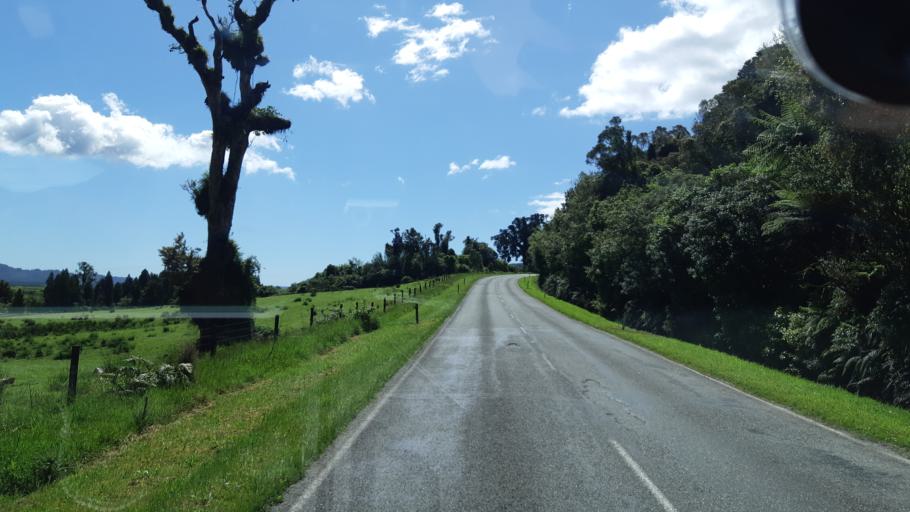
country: NZ
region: West Coast
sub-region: Westland District
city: Hokitika
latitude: -43.0913
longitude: 170.6286
